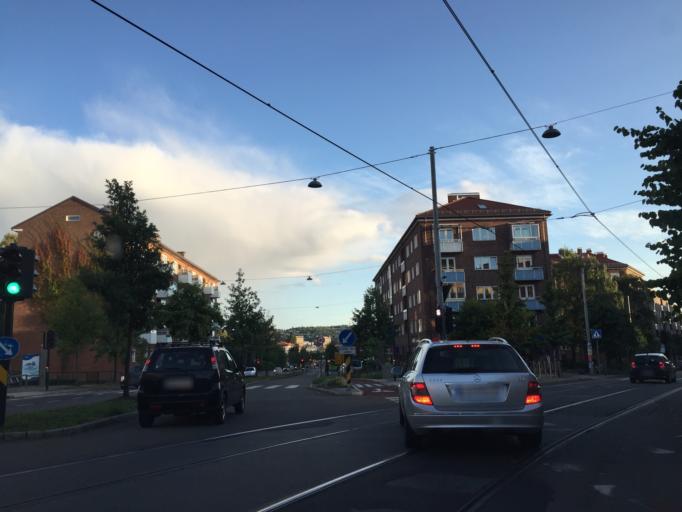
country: NO
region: Oslo
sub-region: Oslo
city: Oslo
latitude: 59.9256
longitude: 10.7759
